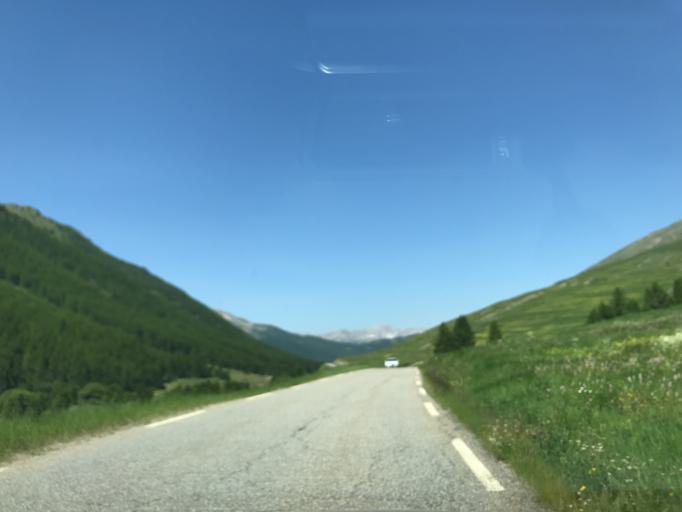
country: IT
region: Piedmont
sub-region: Provincia di Cuneo
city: Pontechianale
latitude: 44.7194
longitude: 6.9025
